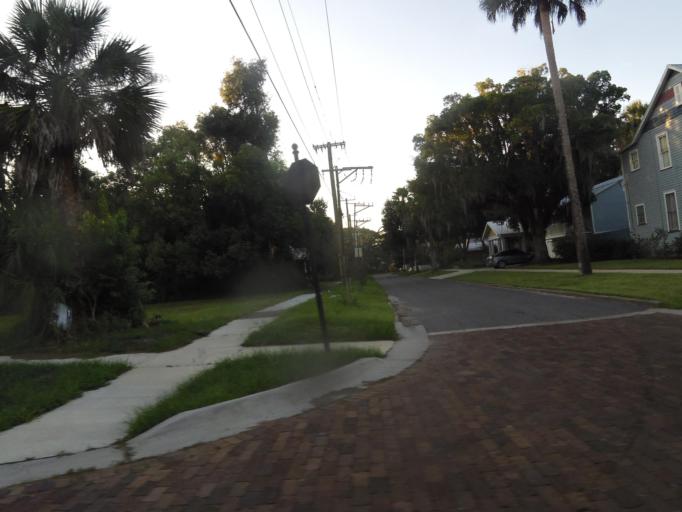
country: US
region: Florida
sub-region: Putnam County
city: Palatka
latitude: 29.6438
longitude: -81.6366
